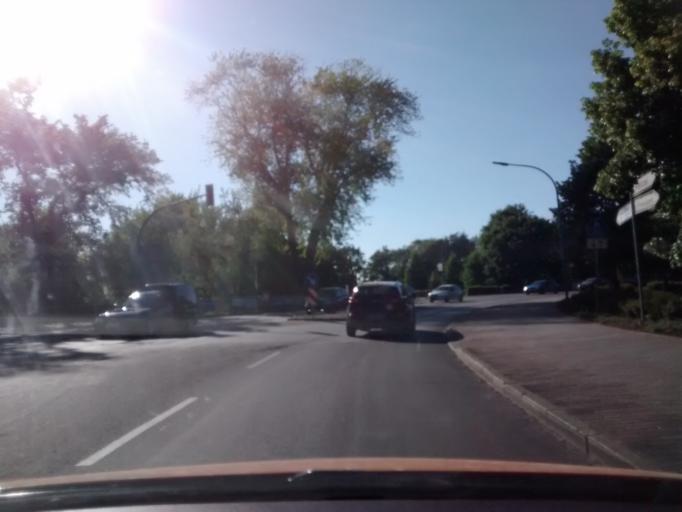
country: DE
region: Brandenburg
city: Furstenwalde
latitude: 52.3535
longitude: 14.0631
